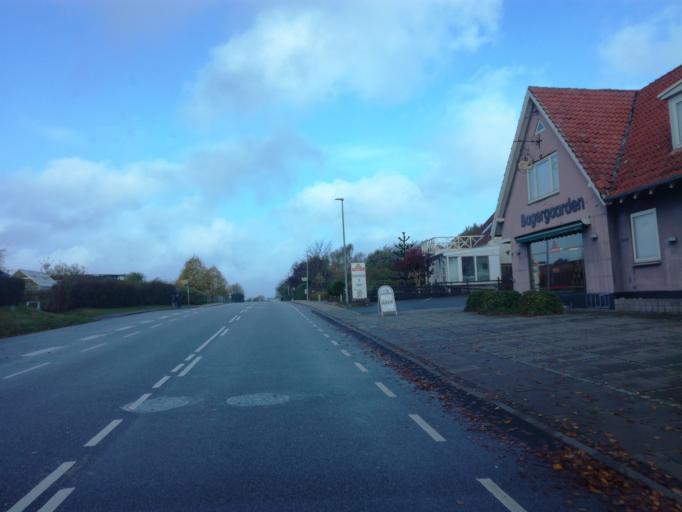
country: DK
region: South Denmark
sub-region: Vejle Kommune
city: Vejle
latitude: 55.6754
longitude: 9.5702
